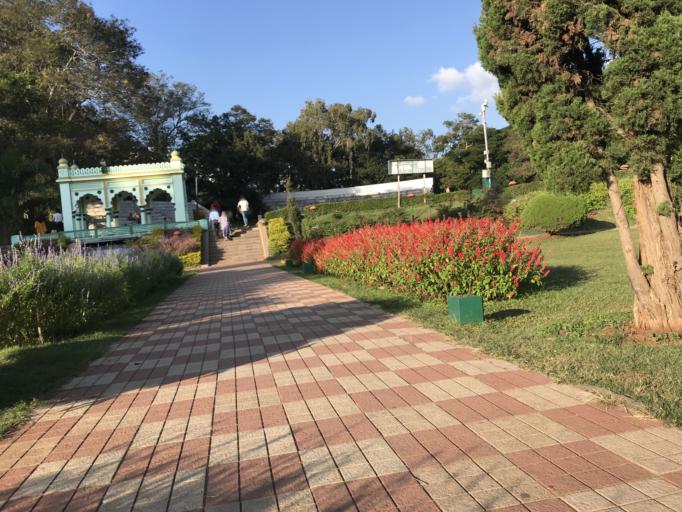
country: IN
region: Karnataka
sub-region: Mandya
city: Shrirangapattana
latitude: 12.4283
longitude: 76.5739
